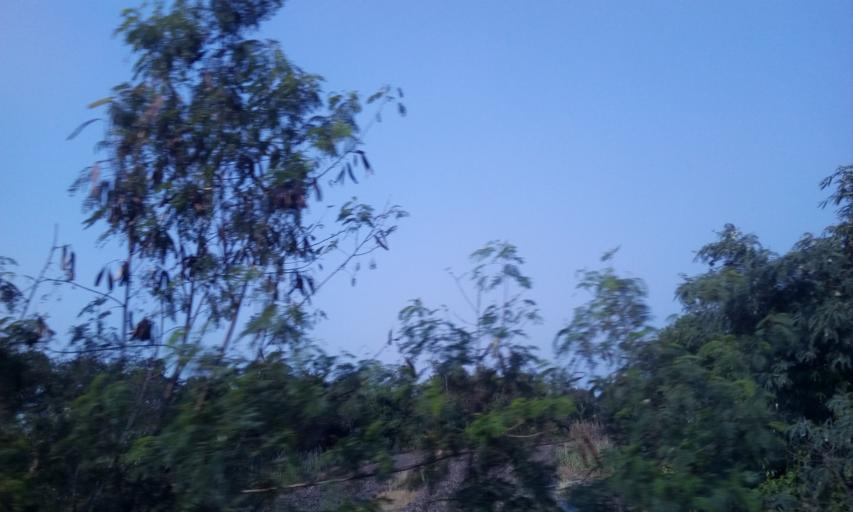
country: TH
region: Nonthaburi
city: Sai Noi
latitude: 13.9731
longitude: 100.3169
